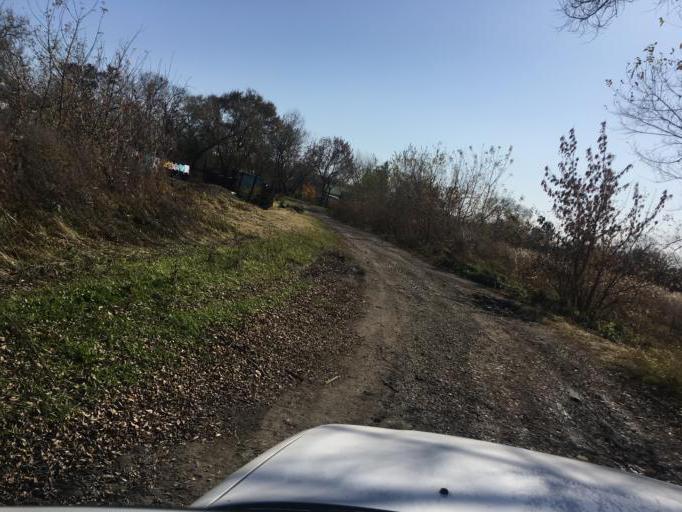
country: RU
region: Primorskiy
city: Dal'nerechensk
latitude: 45.9106
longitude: 133.7933
